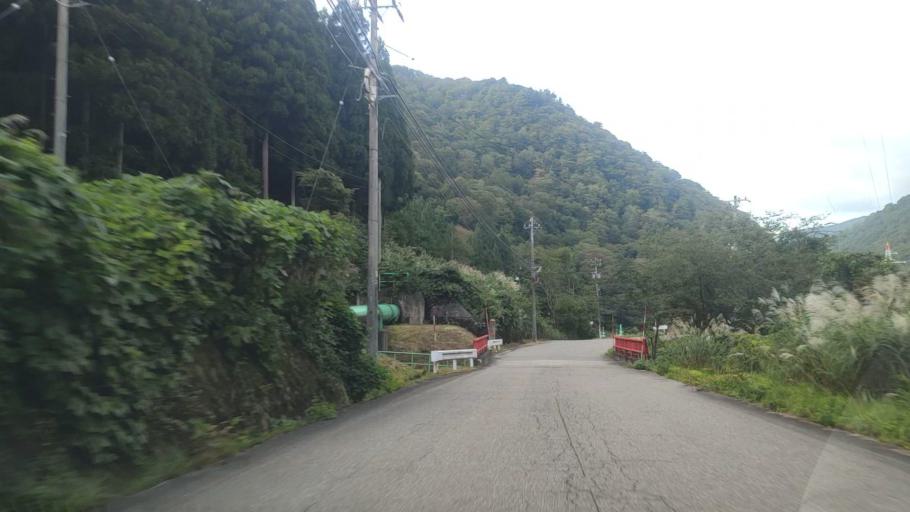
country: JP
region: Toyama
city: Yatsuomachi-higashikumisaka
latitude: 36.4393
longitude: 137.0807
